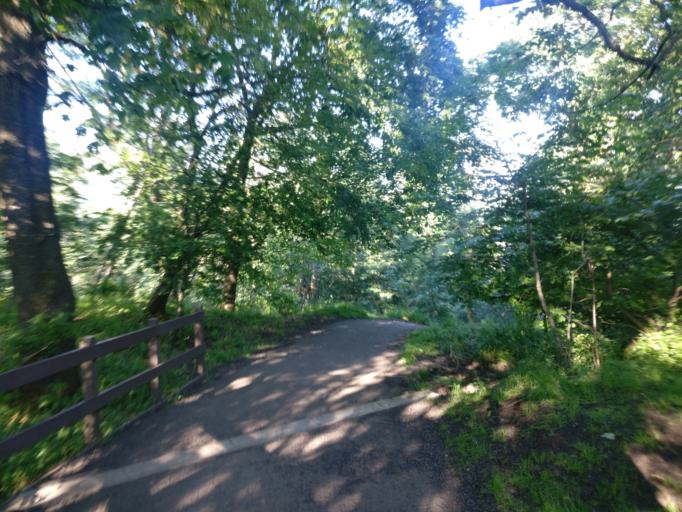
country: GB
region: Scotland
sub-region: Stirling
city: Stirling
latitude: 56.1392
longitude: -3.9176
